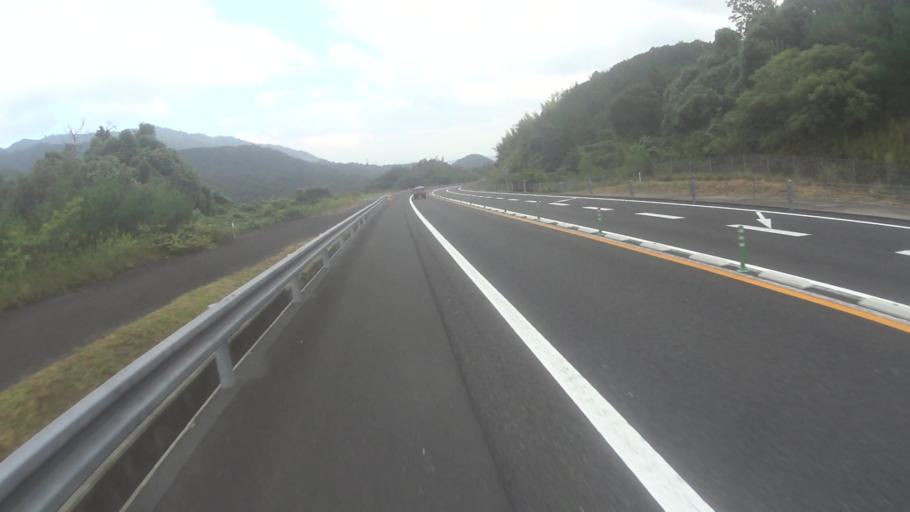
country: JP
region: Kyoto
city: Miyazu
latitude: 35.4956
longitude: 135.1734
